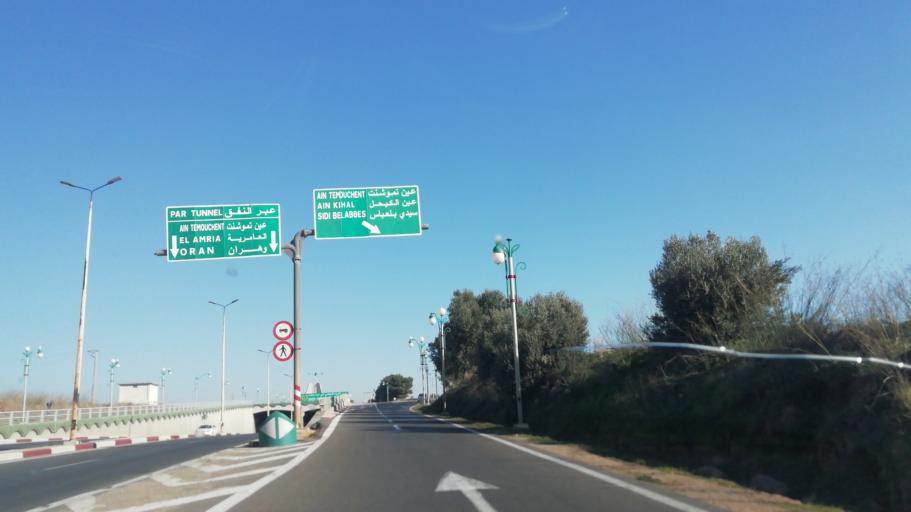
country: DZ
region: Ain Temouchent
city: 'Ain Temouchent
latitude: 35.2999
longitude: -1.1654
